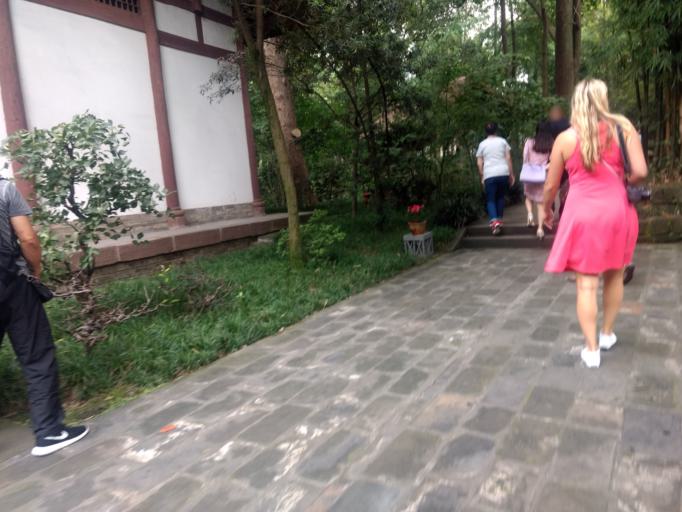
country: CN
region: Sichuan
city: Chengdu
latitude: 30.6629
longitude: 104.0250
